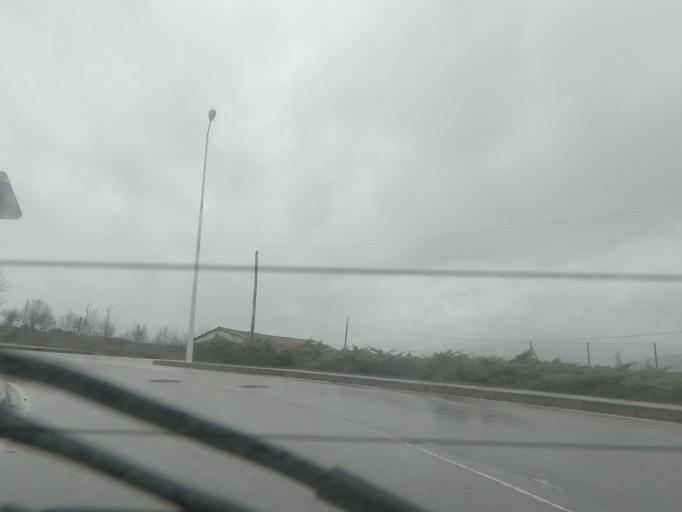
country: PT
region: Vila Real
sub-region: Vila Real
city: Vila Real
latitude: 41.2857
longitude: -7.7347
